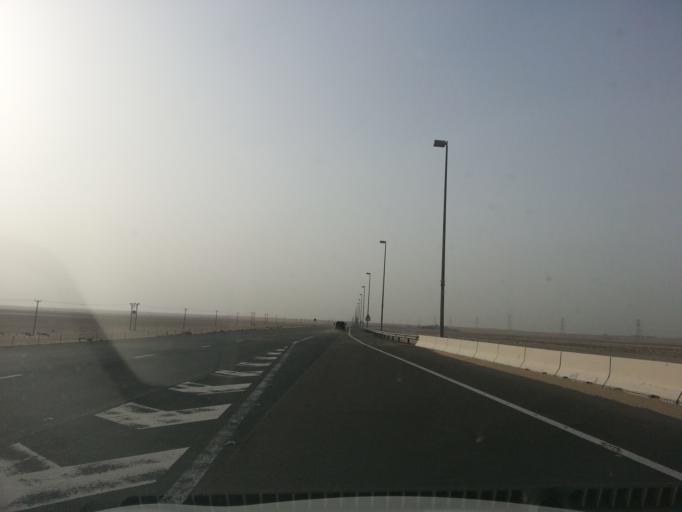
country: AE
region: Dubai
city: Dubai
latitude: 24.7949
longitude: 55.0752
